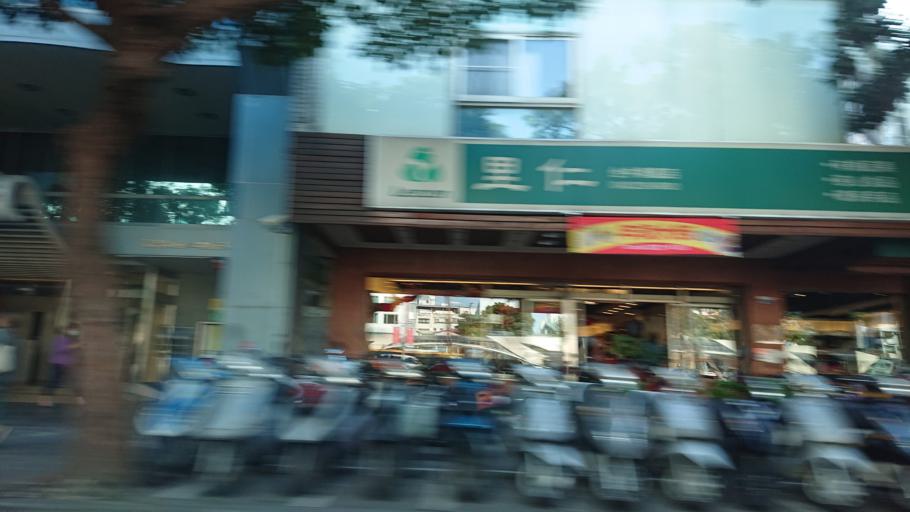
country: TW
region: Taiwan
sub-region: Taichung City
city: Taichung
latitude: 24.1586
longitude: 120.6562
